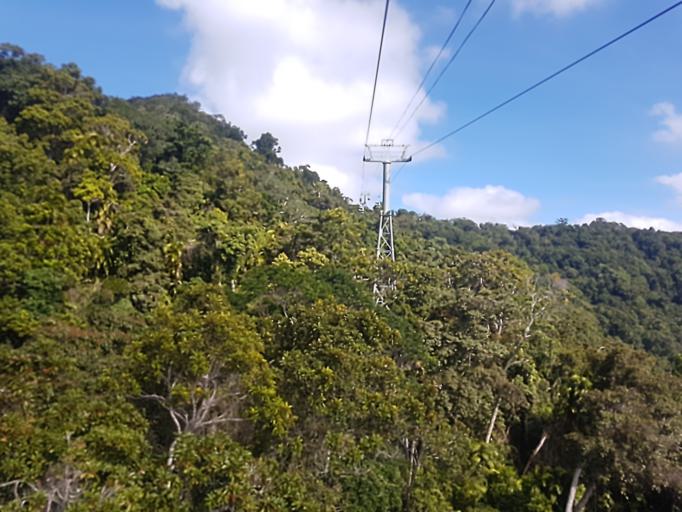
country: AU
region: Queensland
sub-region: Cairns
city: Redlynch
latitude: -16.8489
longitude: 145.6762
